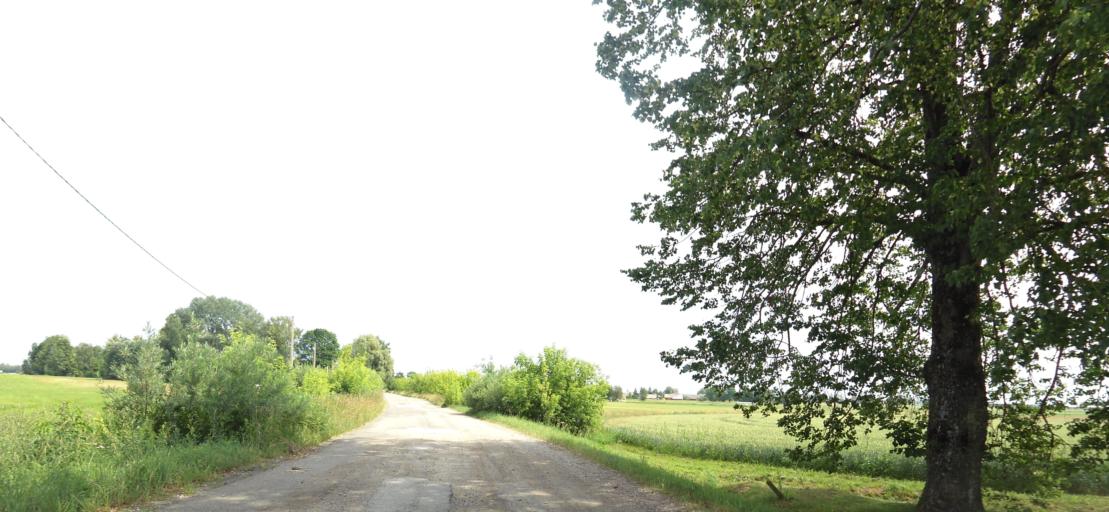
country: LT
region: Panevezys
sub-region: Birzai
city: Birzai
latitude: 56.3237
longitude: 24.7007
